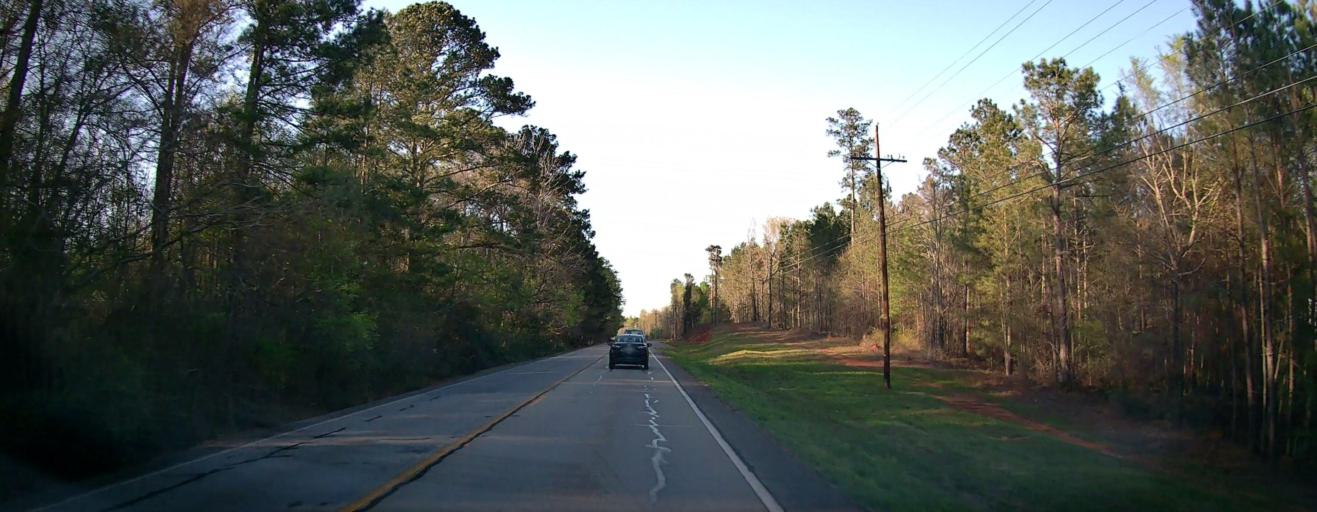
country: US
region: Georgia
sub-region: Newton County
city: Oakwood
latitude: 33.4242
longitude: -83.8952
